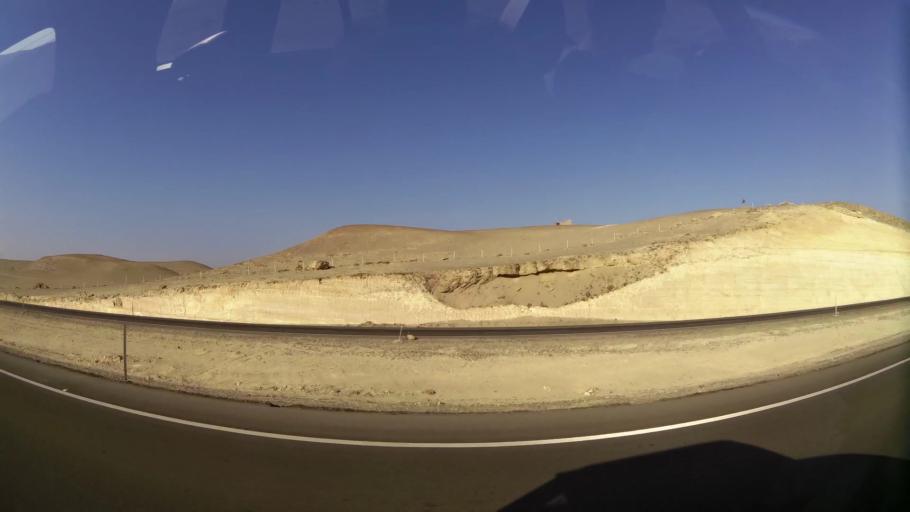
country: PE
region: Ica
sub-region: Provincia de Pisco
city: San Clemente
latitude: -13.6592
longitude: -76.1740
